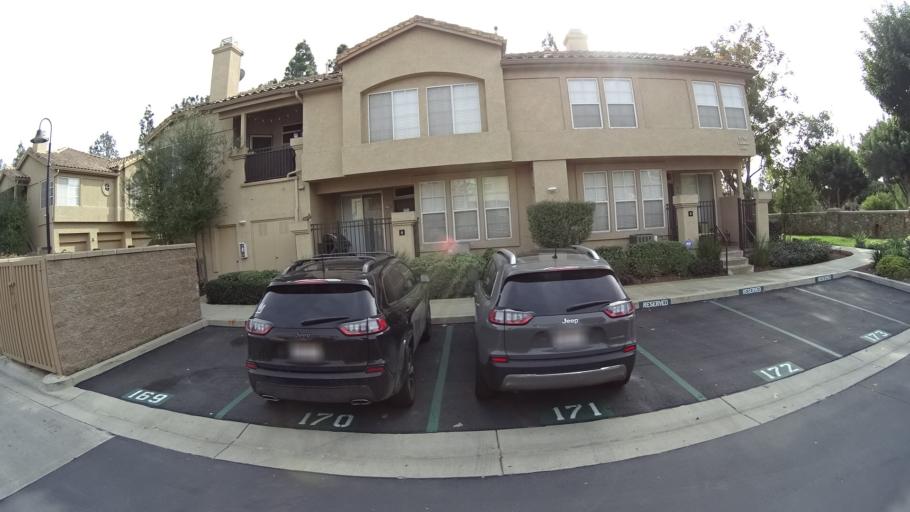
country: US
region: California
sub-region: Orange County
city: Laguna Woods
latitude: 33.6014
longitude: -117.7423
